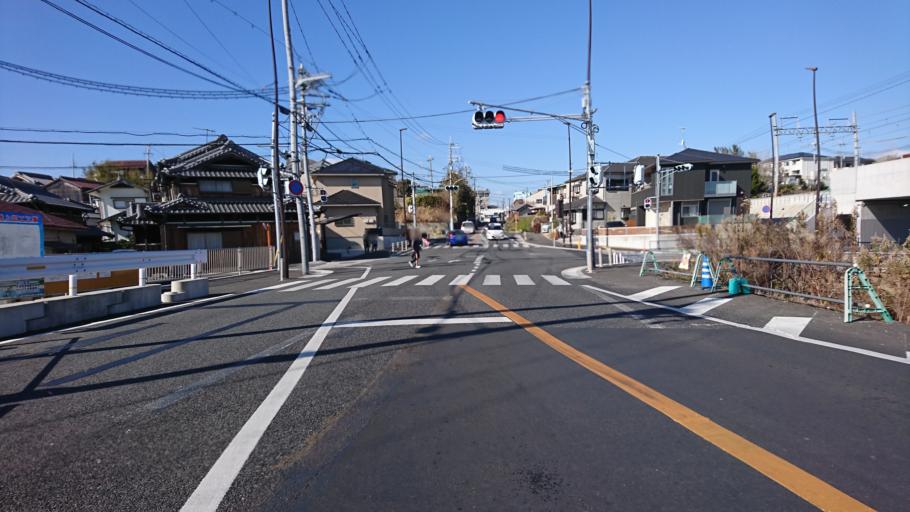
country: JP
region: Hyogo
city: Akashi
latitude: 34.6667
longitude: 134.9418
